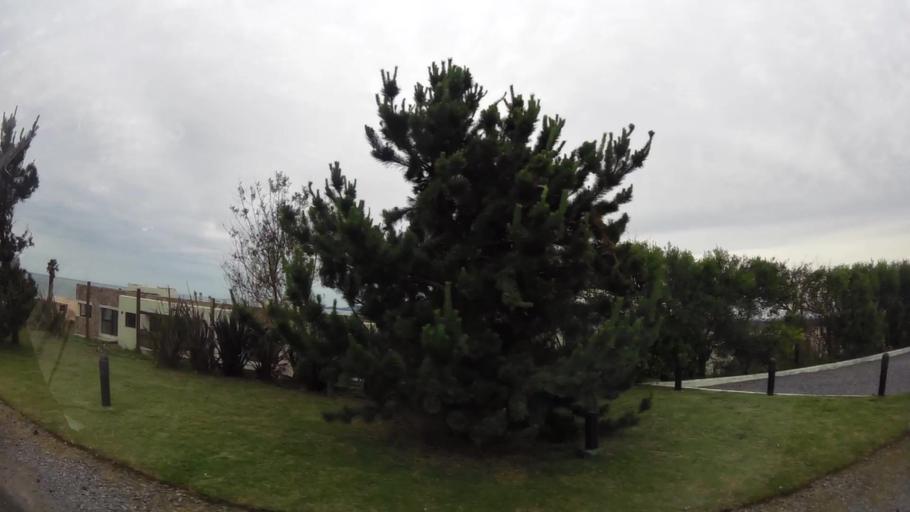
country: UY
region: Maldonado
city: Maldonado
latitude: -34.9018
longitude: -55.0405
